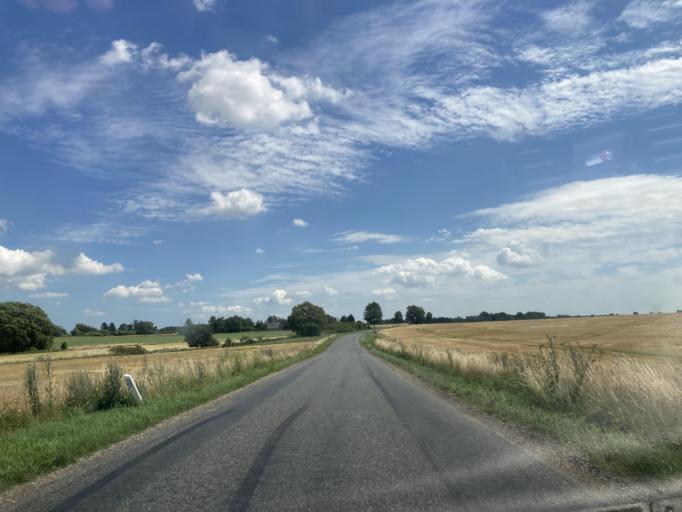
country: DK
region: Zealand
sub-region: Faxe Kommune
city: Haslev
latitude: 55.3828
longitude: 11.9449
